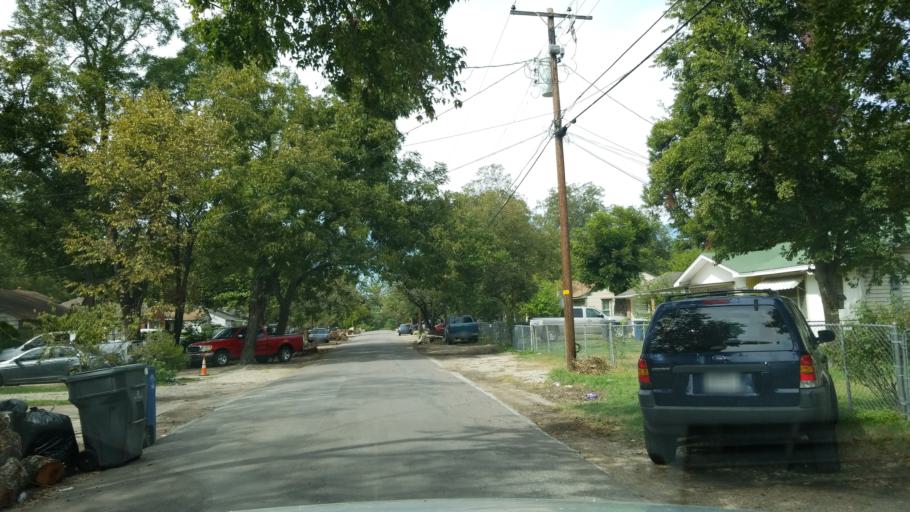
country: US
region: Texas
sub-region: Dallas County
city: Dallas
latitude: 32.7829
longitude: -96.7194
